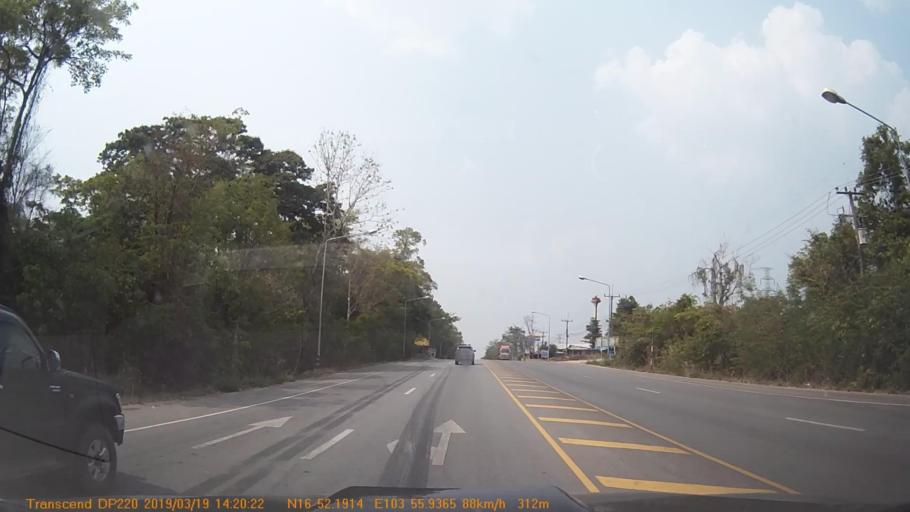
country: TH
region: Sakon Nakhon
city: Phu Phan
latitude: 16.8705
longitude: 103.9322
